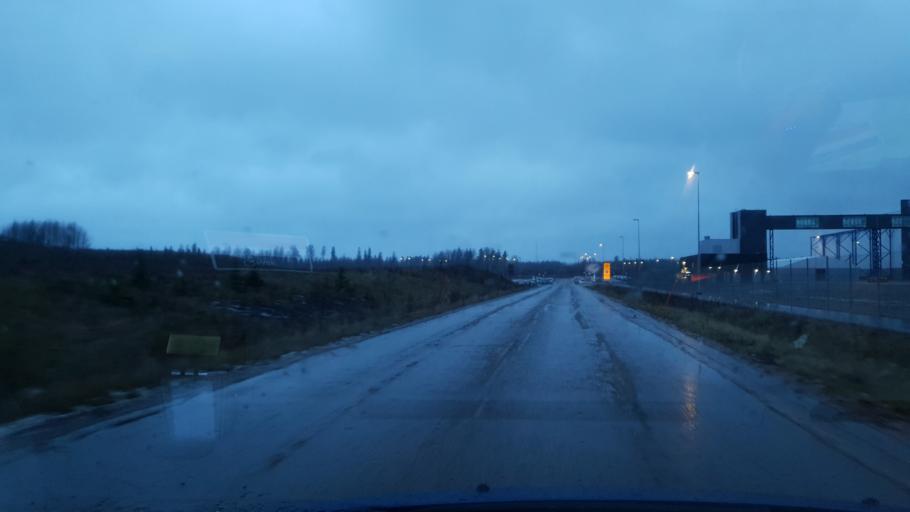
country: FI
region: Uusimaa
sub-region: Helsinki
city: Kerava
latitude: 60.3742
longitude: 25.1527
